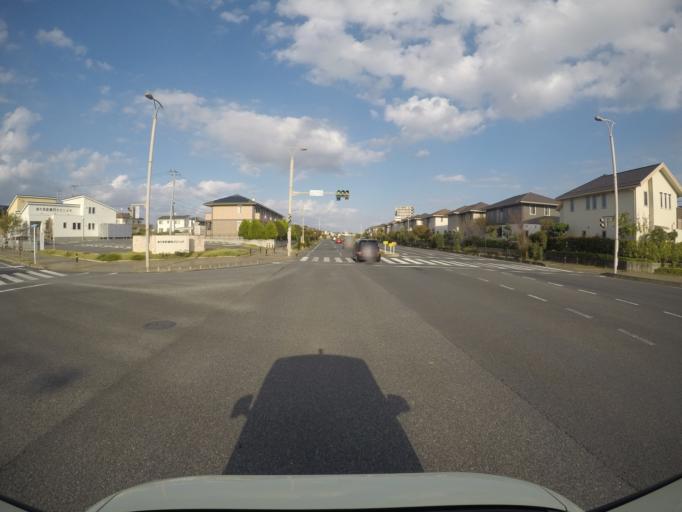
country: JP
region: Ibaraki
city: Mitsukaido
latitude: 35.9978
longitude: 140.0378
